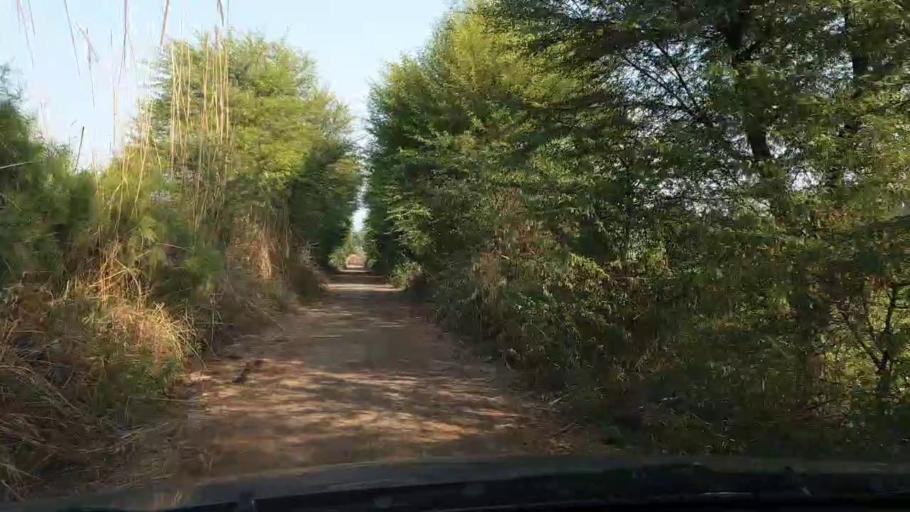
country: PK
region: Sindh
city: Sanghar
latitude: 25.9856
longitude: 68.9497
